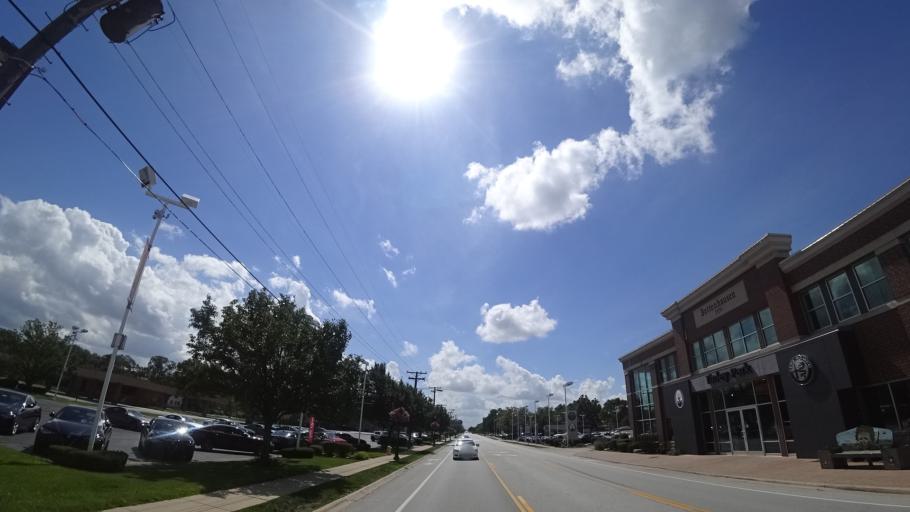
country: US
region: Illinois
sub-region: Cook County
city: Tinley Park
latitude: 41.5725
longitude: -87.7842
